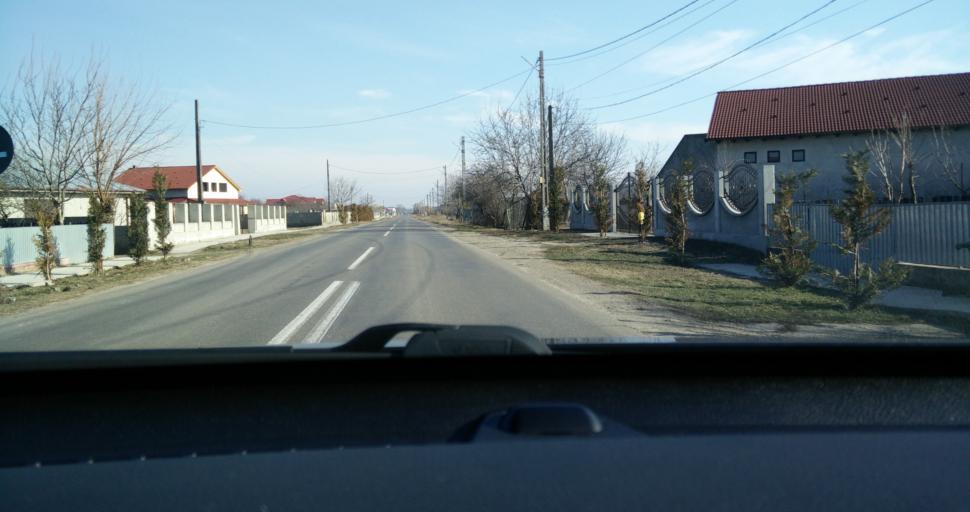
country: RO
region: Vrancea
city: Vulturu de Sus
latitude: 45.6280
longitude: 27.3926
